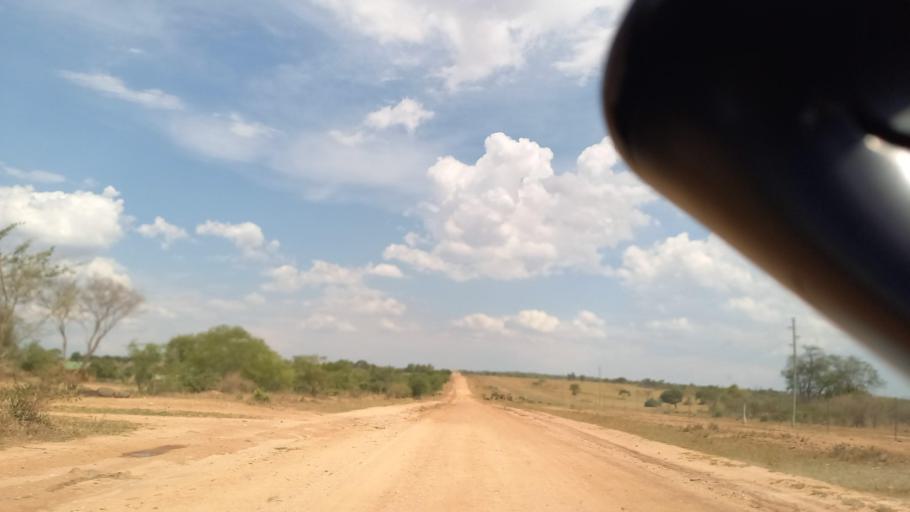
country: ZM
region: Southern
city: Nakambala
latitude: -16.1084
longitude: 28.0247
